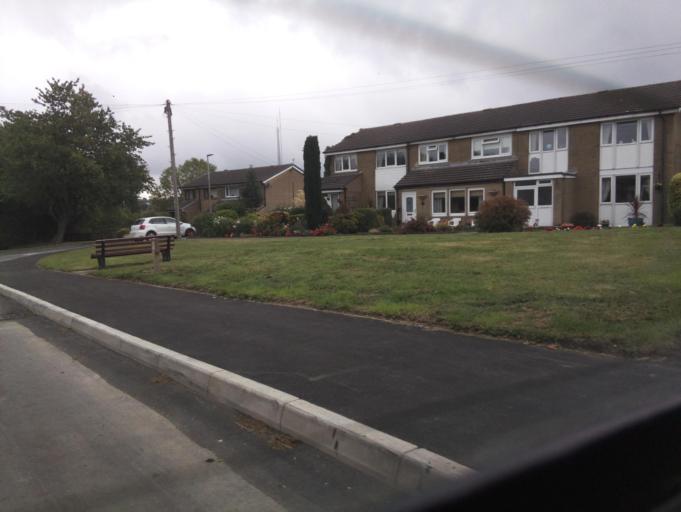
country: GB
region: England
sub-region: Kirklees
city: Shelley
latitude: 53.5976
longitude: -1.6845
